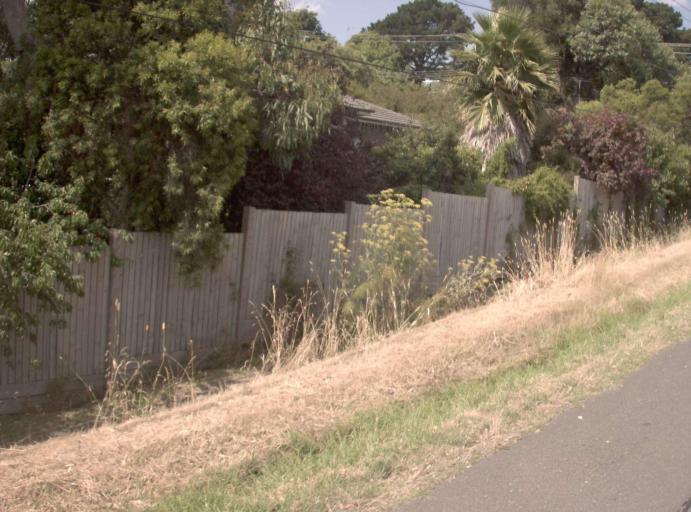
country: AU
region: Victoria
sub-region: Knox
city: Ferntree Gully
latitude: -37.9004
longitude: 145.2921
